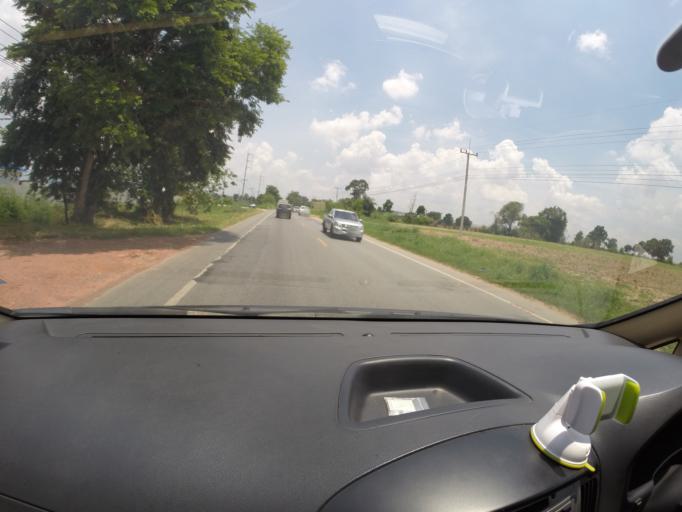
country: TH
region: Nakhon Ratchasima
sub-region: Amphoe Thepharak
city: Thepharak
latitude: 15.1260
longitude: 101.5439
